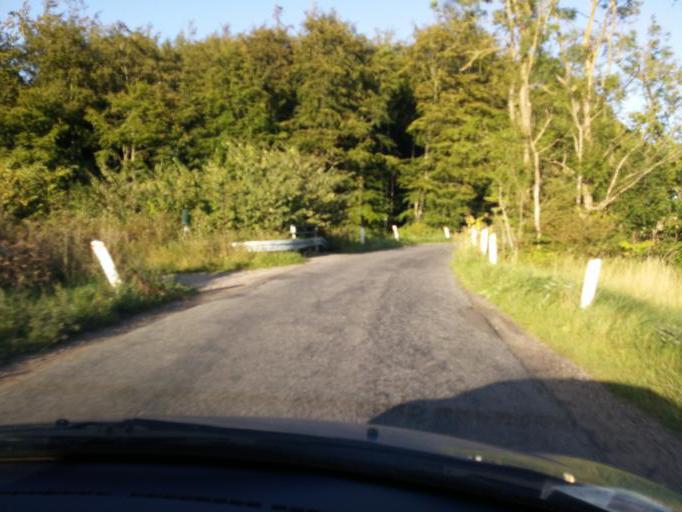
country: DK
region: South Denmark
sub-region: Kerteminde Kommune
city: Munkebo
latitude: 55.4237
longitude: 10.5512
